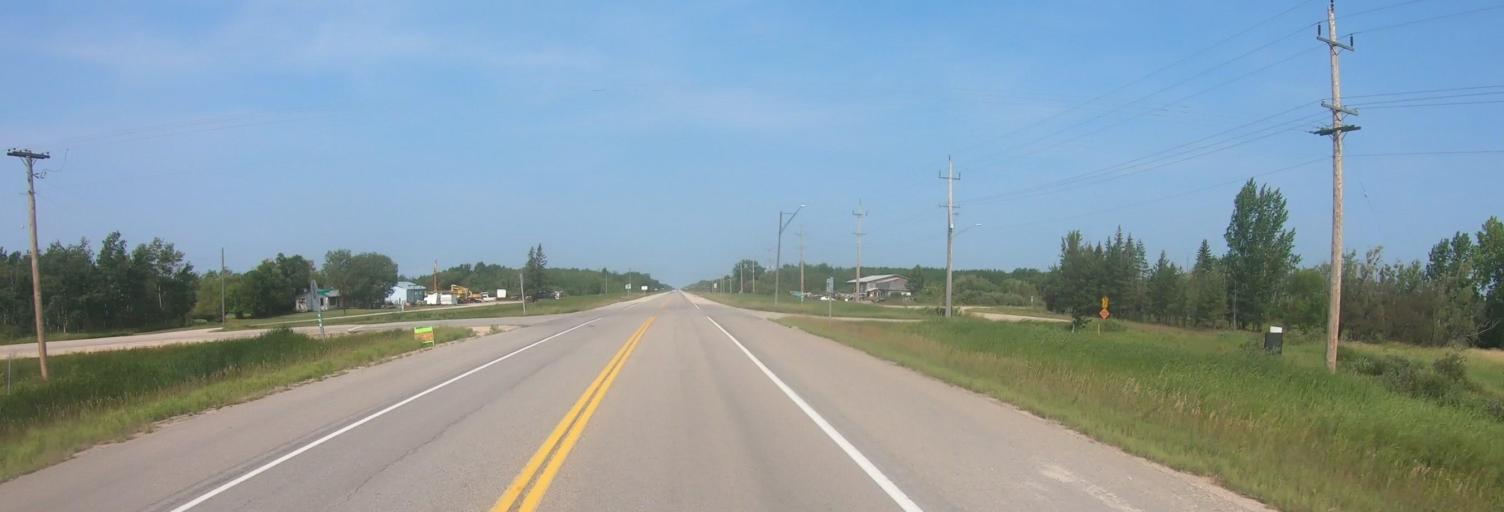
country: CA
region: Manitoba
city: La Broquerie
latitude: 49.2835
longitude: -96.5091
